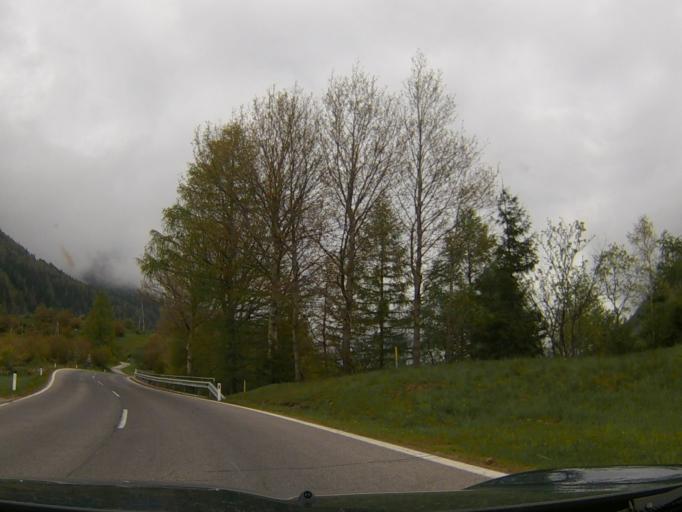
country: AT
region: Carinthia
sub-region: Politischer Bezirk Spittal an der Drau
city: Obervellach
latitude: 46.9705
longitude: 13.1832
